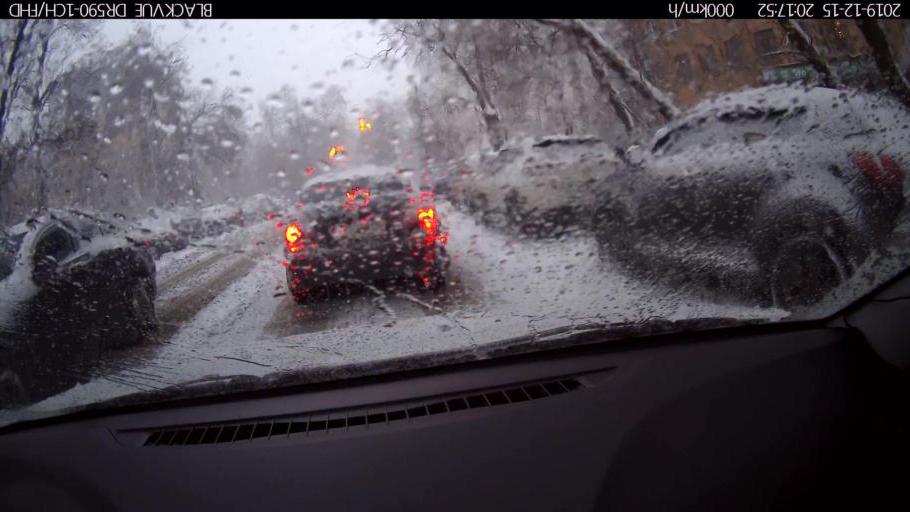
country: RU
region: Nizjnij Novgorod
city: Nizhniy Novgorod
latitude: 56.3148
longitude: 44.0264
